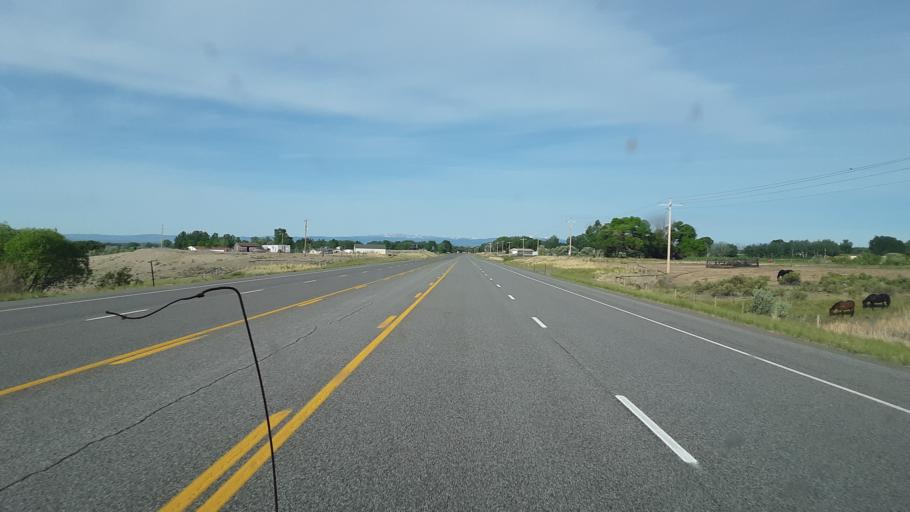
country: US
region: Wyoming
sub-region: Fremont County
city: Riverton
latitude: 43.1134
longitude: -108.3346
